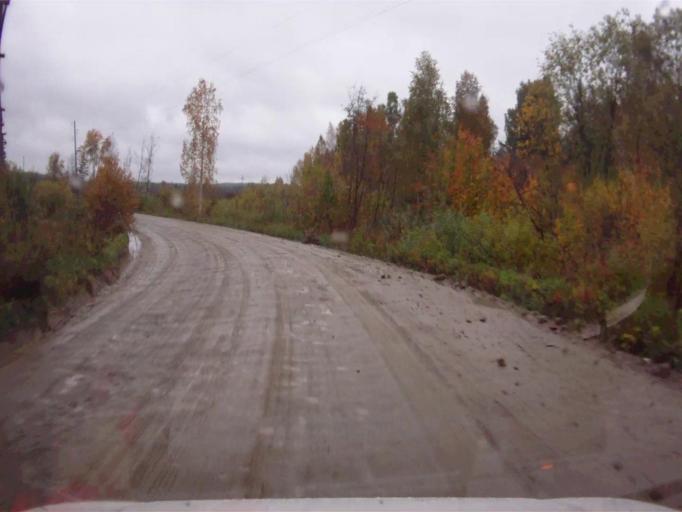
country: RU
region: Chelyabinsk
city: Kyshtym
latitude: 55.7313
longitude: 60.5197
